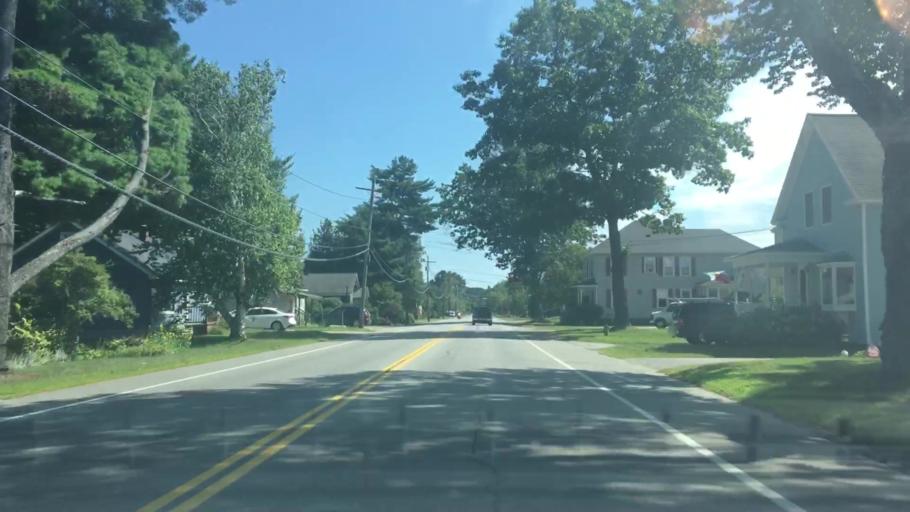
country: US
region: Maine
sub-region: Androscoggin County
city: Sabattus
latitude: 44.0999
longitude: -70.1593
